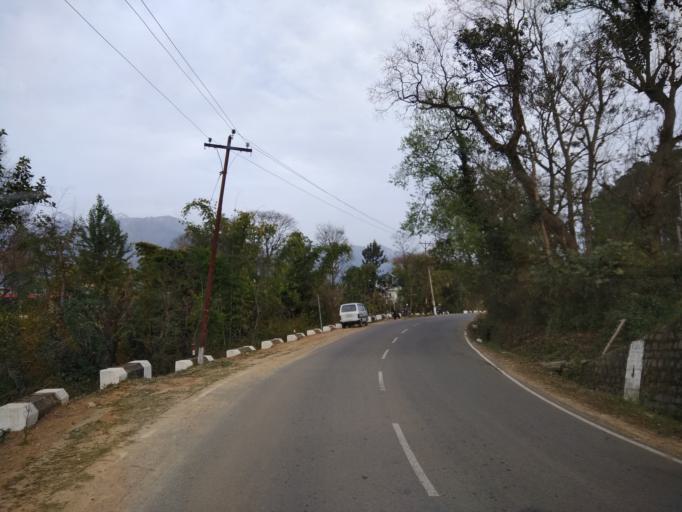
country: IN
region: Himachal Pradesh
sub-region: Kangra
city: Palampur
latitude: 32.1150
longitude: 76.5127
